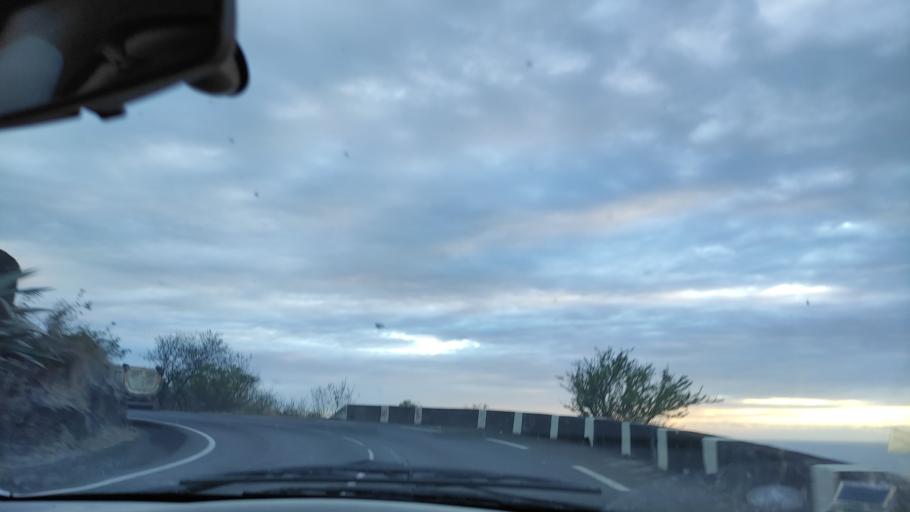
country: RE
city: Piton Saint-Leu
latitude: -21.2036
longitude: 55.2940
